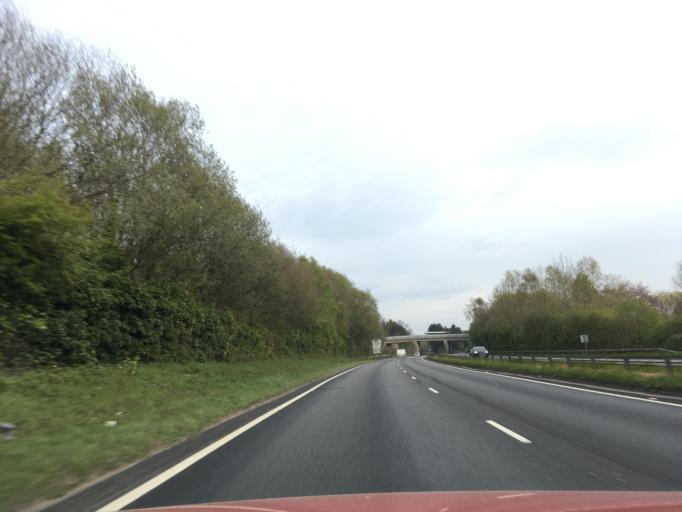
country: GB
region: Wales
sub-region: Caerphilly County Borough
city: Risca
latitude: 51.5913
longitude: -3.0627
